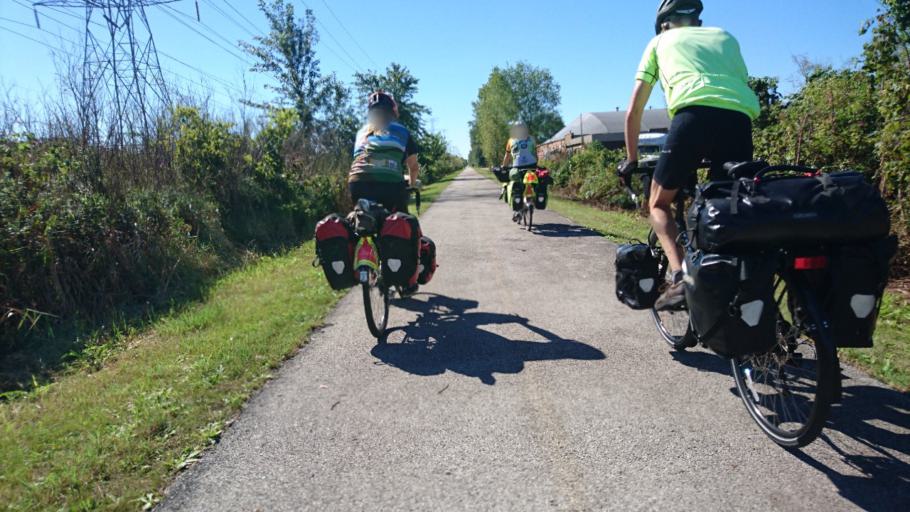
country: US
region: Illinois
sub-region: Cook County
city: Burnham
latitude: 41.6221
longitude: -87.5495
